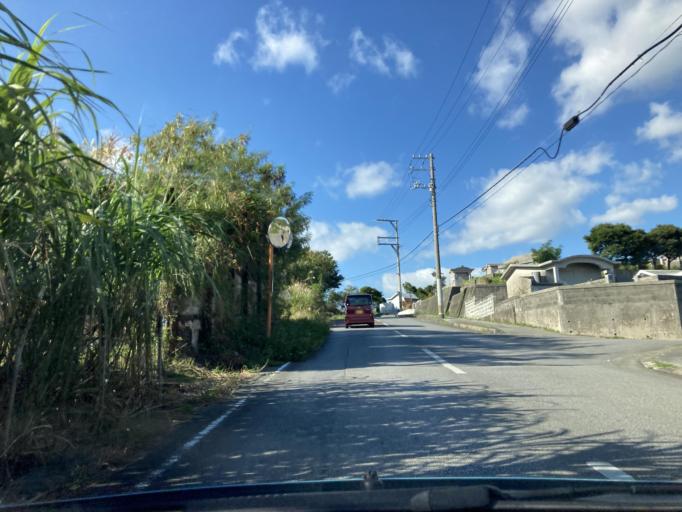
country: JP
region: Okinawa
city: Ginowan
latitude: 26.2172
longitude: 127.7517
